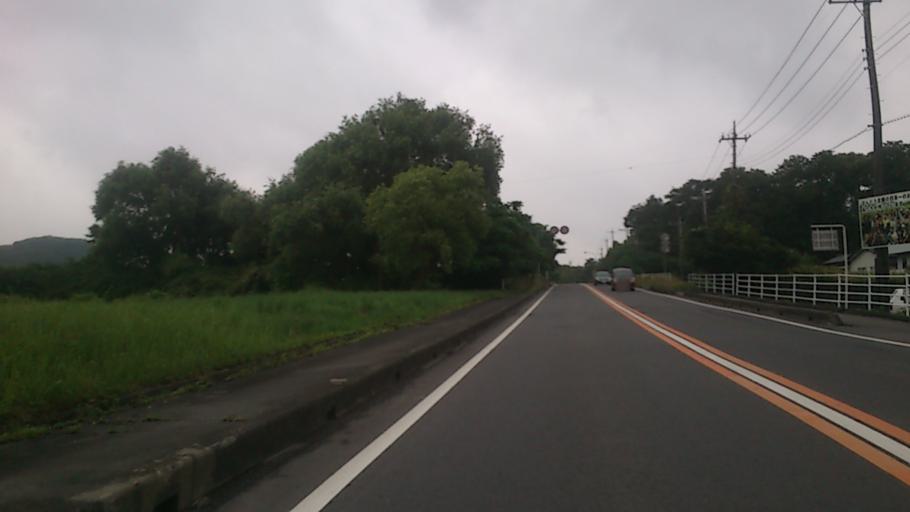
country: JP
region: Ibaraki
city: Omiya
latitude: 36.6235
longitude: 140.4031
